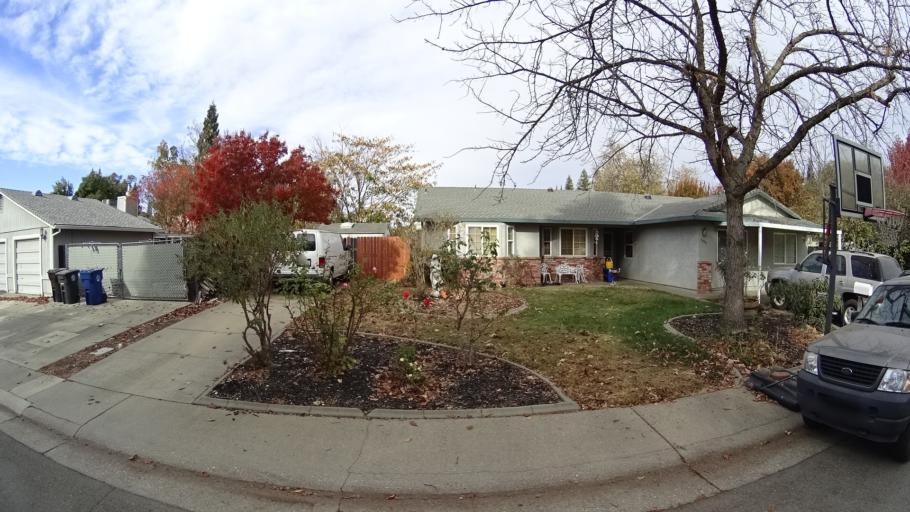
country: US
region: California
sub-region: Sacramento County
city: Citrus Heights
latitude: 38.7036
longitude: -121.2685
